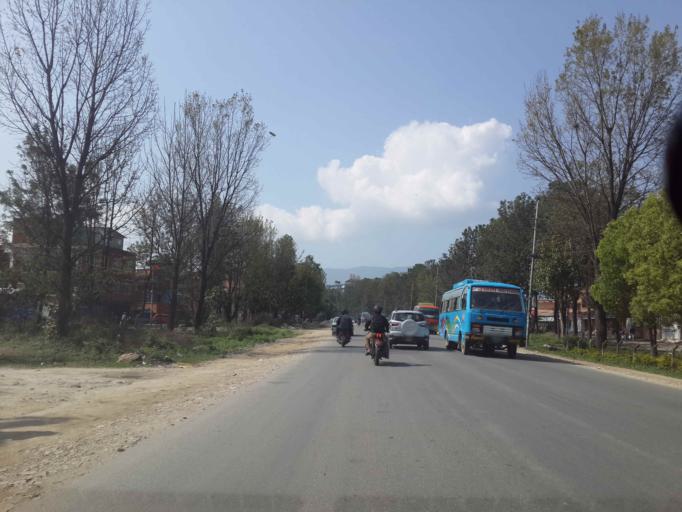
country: NP
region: Central Region
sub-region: Bagmati Zone
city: Kathmandu
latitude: 27.7362
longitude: 85.3417
